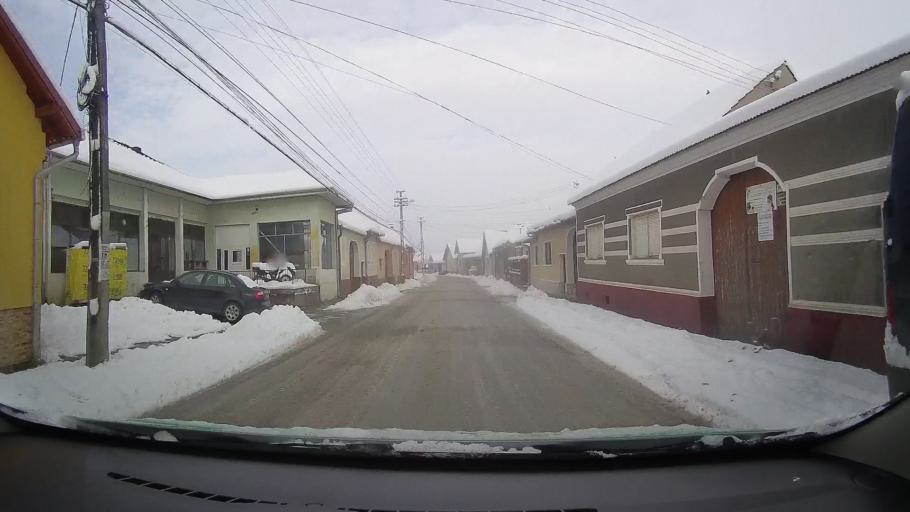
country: RO
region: Alba
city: Pianu de Sus
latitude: 45.9017
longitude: 23.4805
